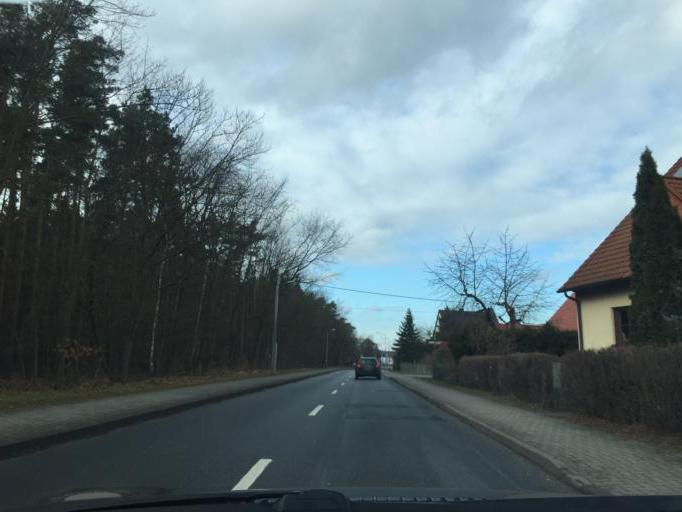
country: DE
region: Saxony
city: Ottendorf-Okrilla
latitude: 51.1745
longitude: 13.8290
